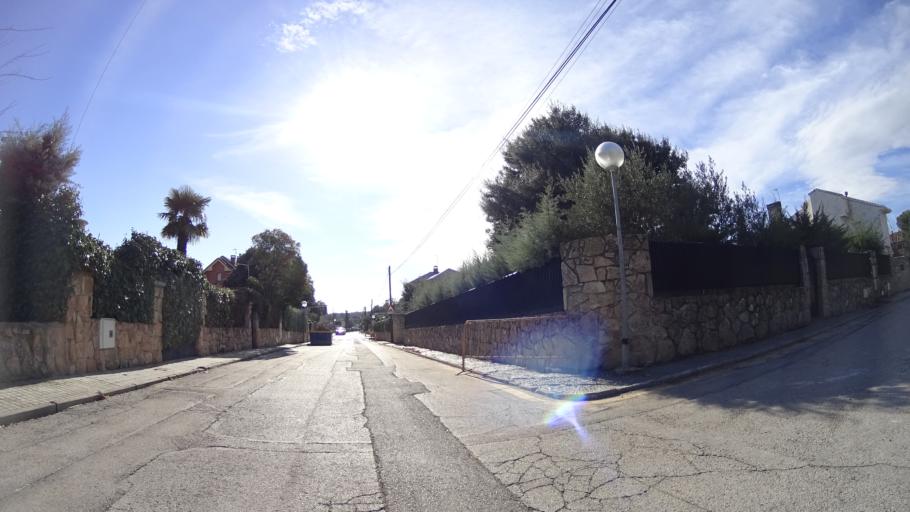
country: ES
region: Madrid
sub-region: Provincia de Madrid
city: Galapagar
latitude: 40.5792
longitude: -4.0199
